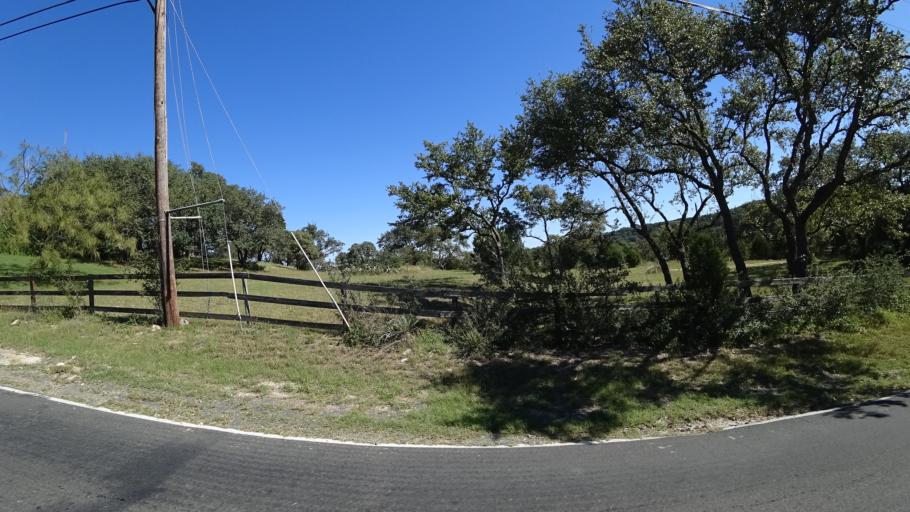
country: US
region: Texas
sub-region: Travis County
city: West Lake Hills
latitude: 30.3109
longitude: -97.8021
